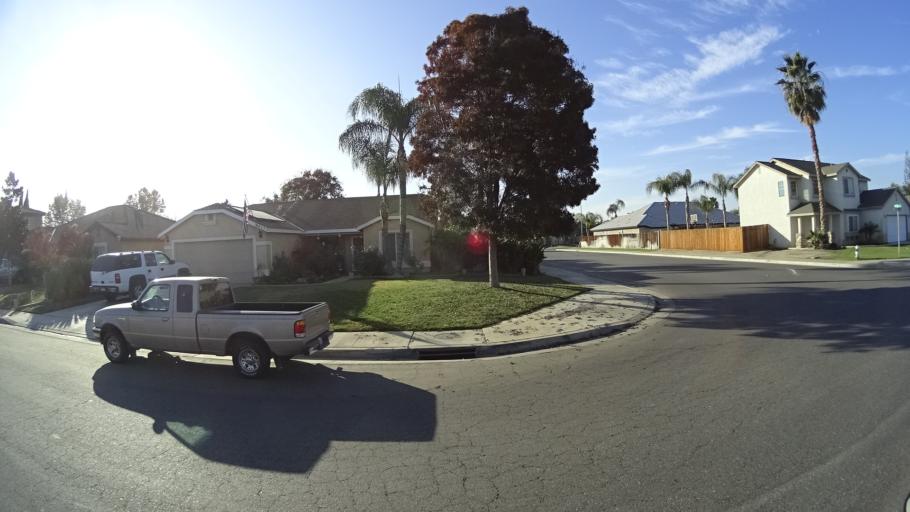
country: US
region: California
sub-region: Kern County
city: Greenfield
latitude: 35.2782
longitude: -119.0506
